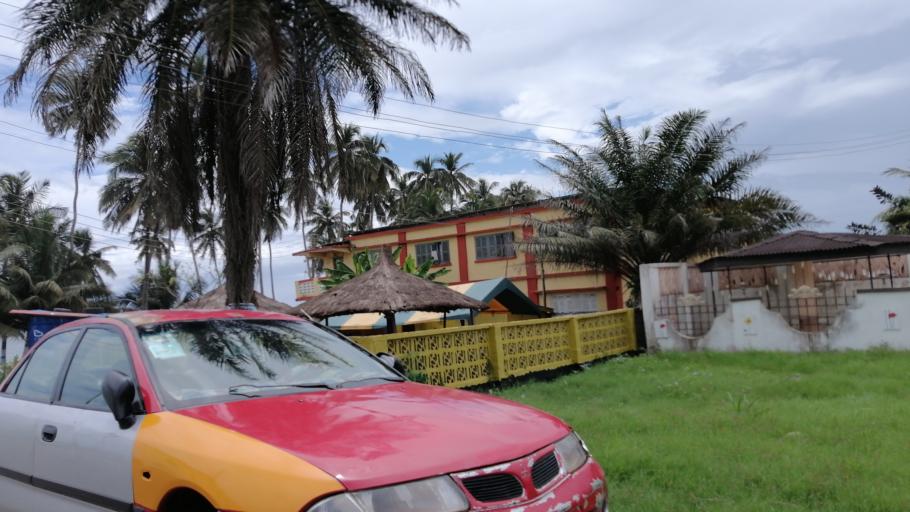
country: GH
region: Central
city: Elmina
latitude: 5.0912
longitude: -1.3454
